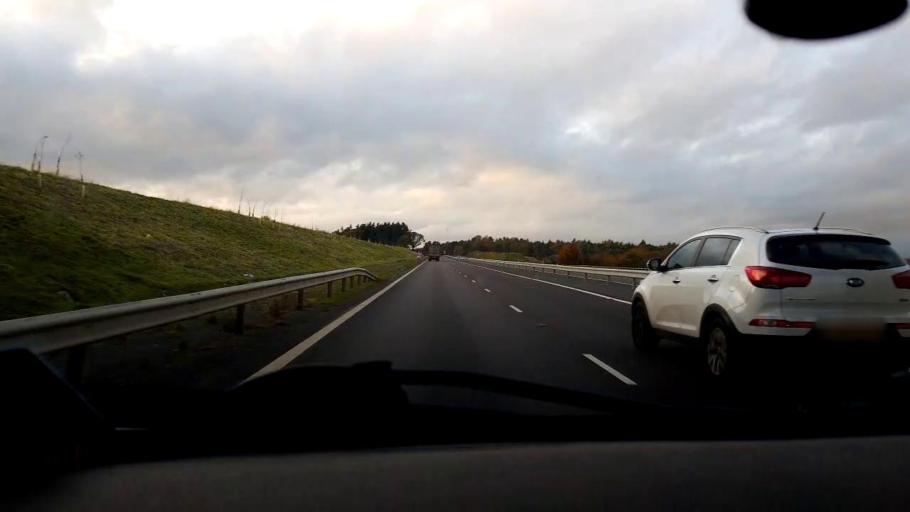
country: GB
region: England
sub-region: Norfolk
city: Horsford
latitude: 52.6931
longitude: 1.2246
